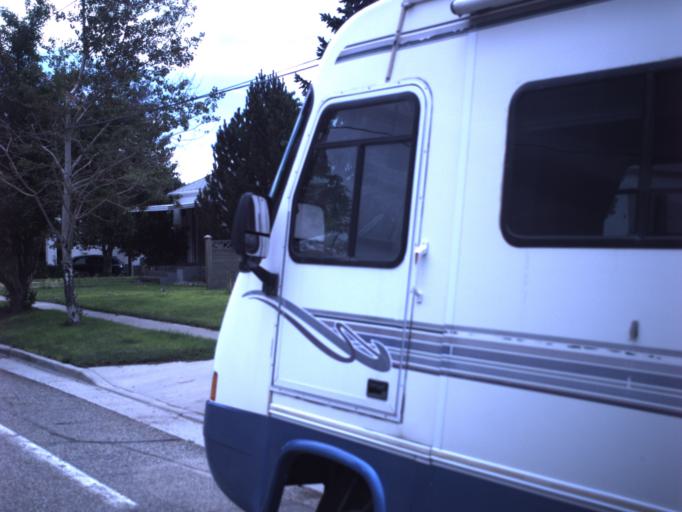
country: US
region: Utah
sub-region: Salt Lake County
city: Herriman
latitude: 40.5641
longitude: -112.1045
